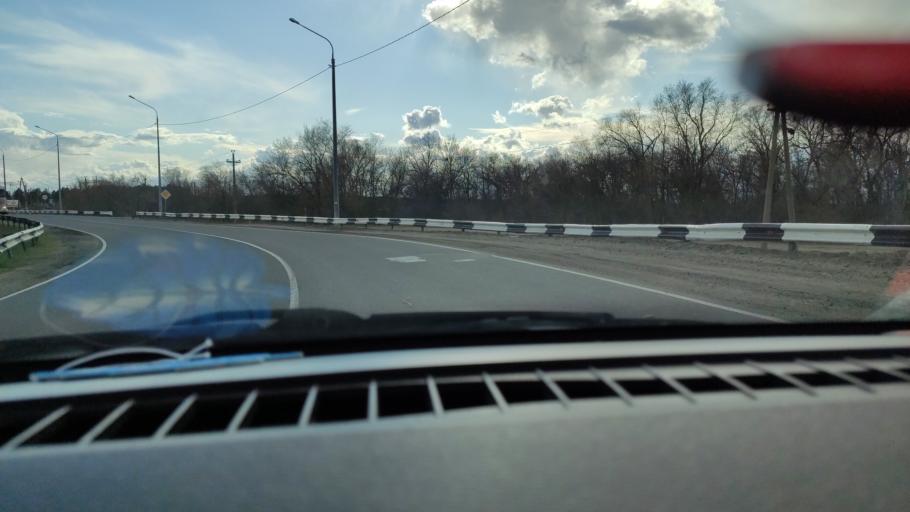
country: RU
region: Saratov
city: Sennoy
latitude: 52.1511
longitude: 46.9500
